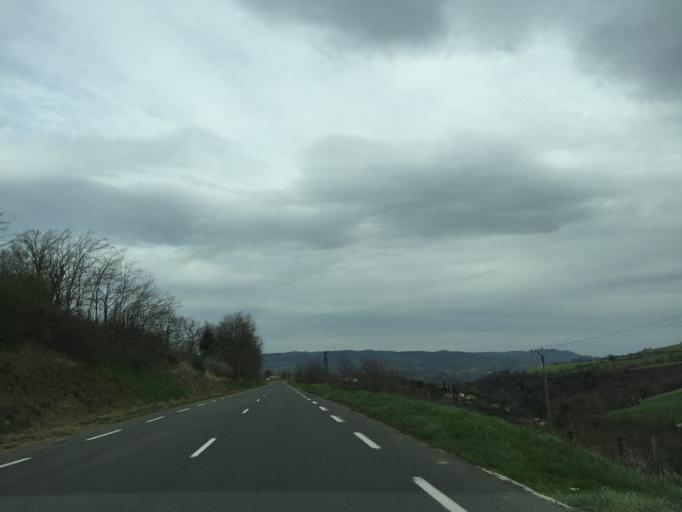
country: FR
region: Rhone-Alpes
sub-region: Departement de la Loire
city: Saint-Paul-en-Jarez
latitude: 45.4698
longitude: 4.5846
